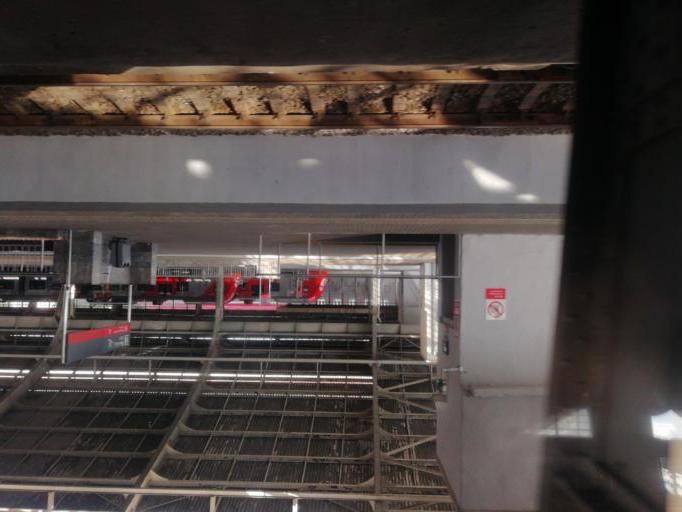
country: RU
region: Kaliningrad
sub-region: Gorod Kaliningrad
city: Kaliningrad
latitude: 54.6937
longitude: 20.4975
